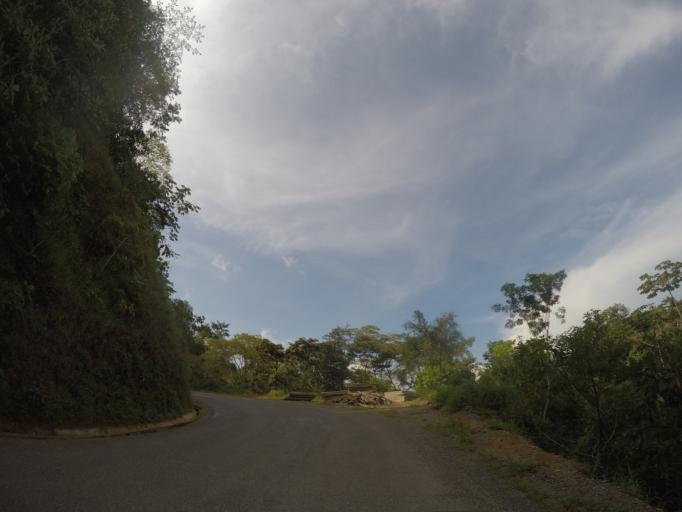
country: MX
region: Oaxaca
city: Pluma Hidalgo
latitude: 15.9343
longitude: -96.4308
